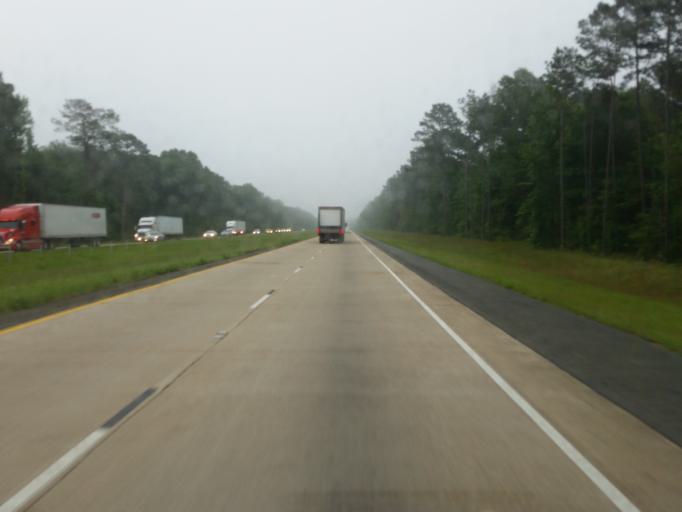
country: US
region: Louisiana
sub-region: Webster Parish
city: Sibley
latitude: 32.5851
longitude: -93.3658
